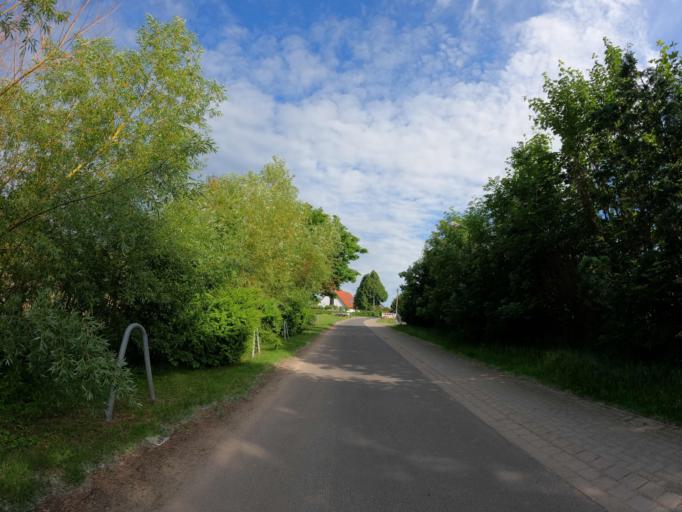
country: DE
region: Mecklenburg-Vorpommern
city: Preetz
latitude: 54.3465
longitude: 13.0088
